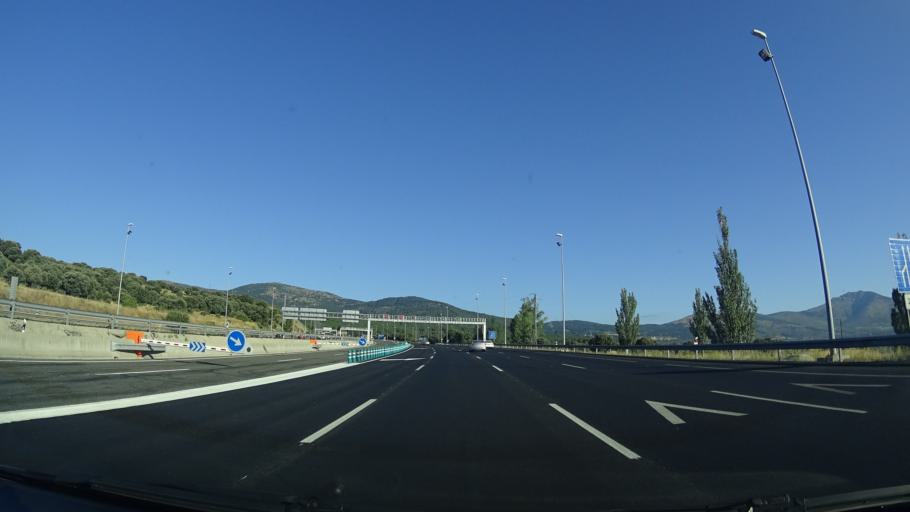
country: ES
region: Madrid
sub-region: Provincia de Madrid
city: Guadarrama
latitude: 40.6675
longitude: -4.1027
